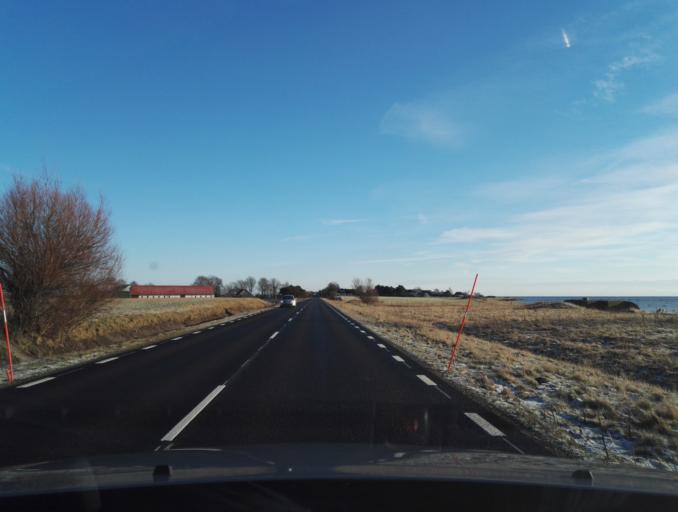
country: SE
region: Skane
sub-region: Trelleborgs Kommun
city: Skare
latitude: 55.3798
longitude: 13.0406
